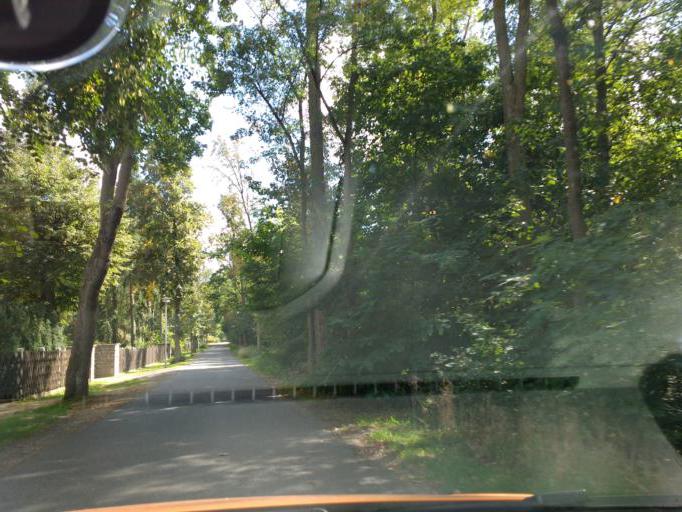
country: DE
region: Brandenburg
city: Storkow
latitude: 52.2333
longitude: 13.9680
